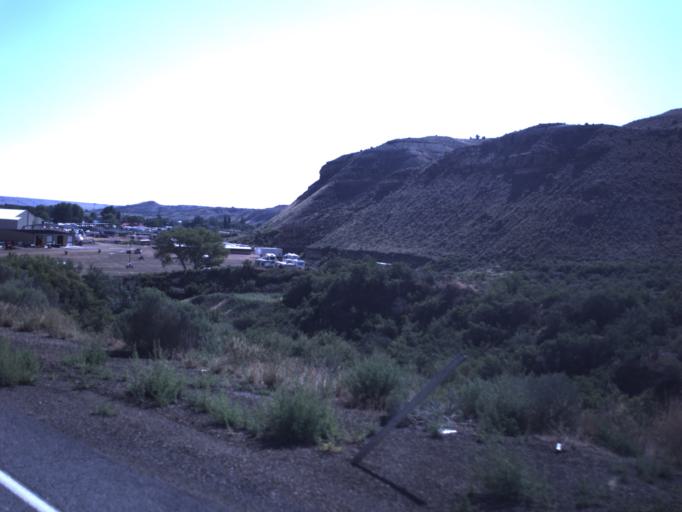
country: US
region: Utah
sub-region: Duchesne County
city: Duchesne
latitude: 40.1560
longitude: -110.4084
